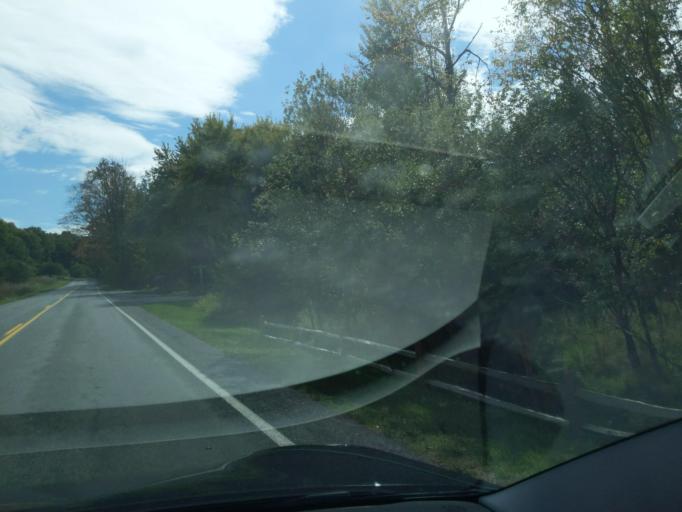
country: US
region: Michigan
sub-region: Antrim County
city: Bellaire
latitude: 45.0122
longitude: -85.2922
